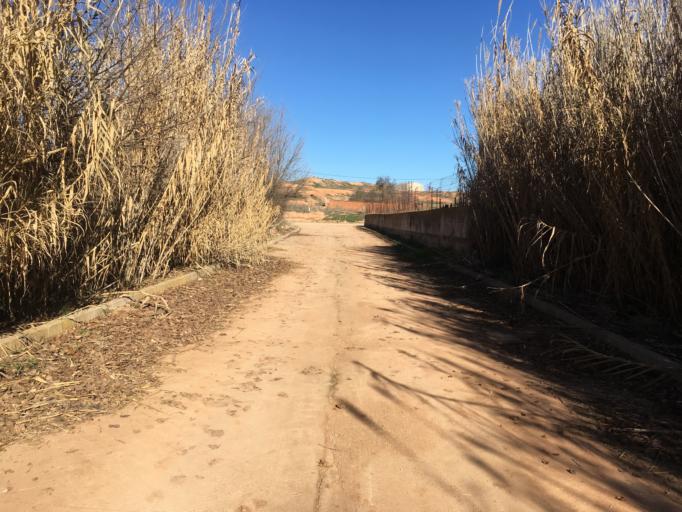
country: ES
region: Castille-La Mancha
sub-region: Provincia de Cuenca
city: Atalaya del Canavate
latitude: 39.5467
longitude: -2.2470
